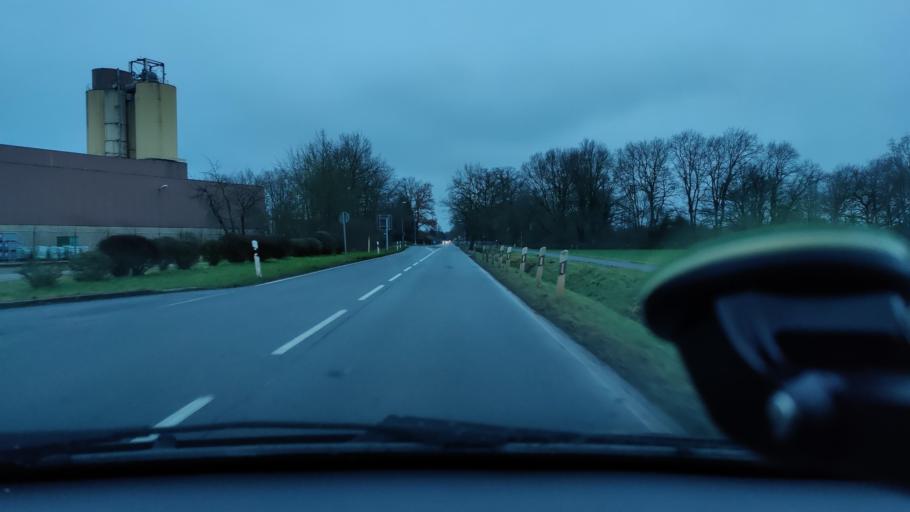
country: DE
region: North Rhine-Westphalia
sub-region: Regierungsbezirk Dusseldorf
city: Xanten
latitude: 51.6577
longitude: 6.4308
